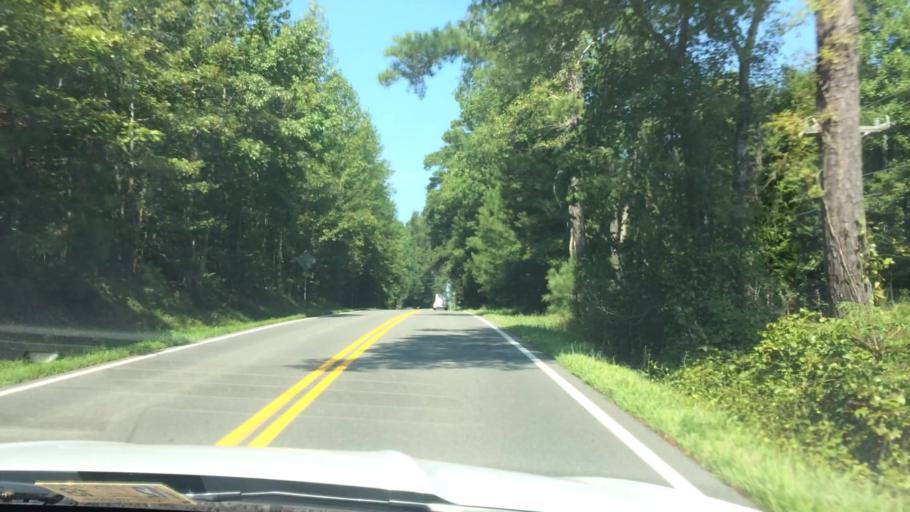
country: US
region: Virginia
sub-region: New Kent County
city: New Kent
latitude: 37.5194
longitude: -76.9987
